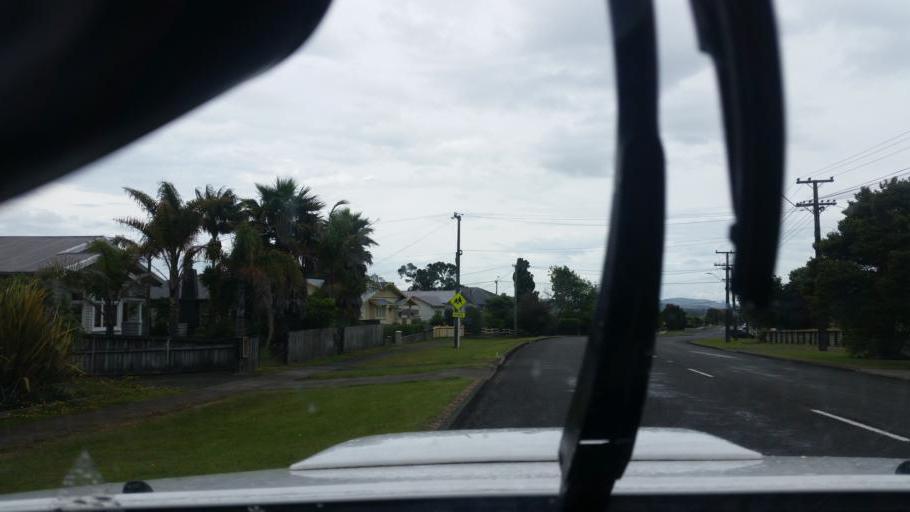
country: NZ
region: Northland
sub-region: Kaipara District
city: Dargaville
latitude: -35.9339
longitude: 173.8606
